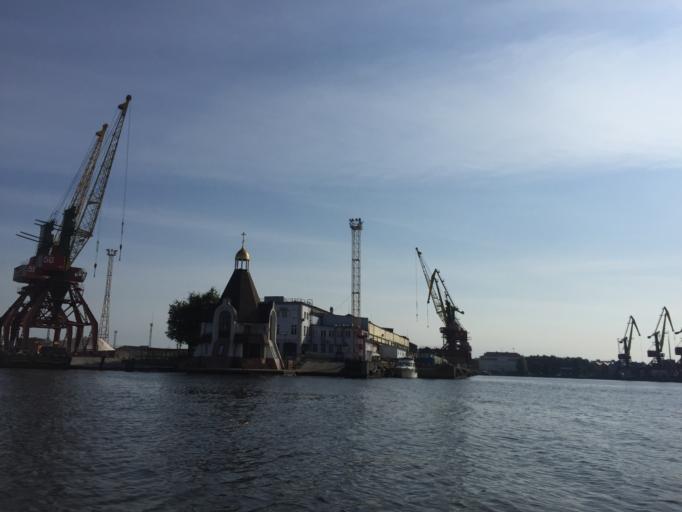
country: RU
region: Kaliningrad
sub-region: Gorod Kaliningrad
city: Kaliningrad
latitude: 54.7044
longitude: 20.4734
